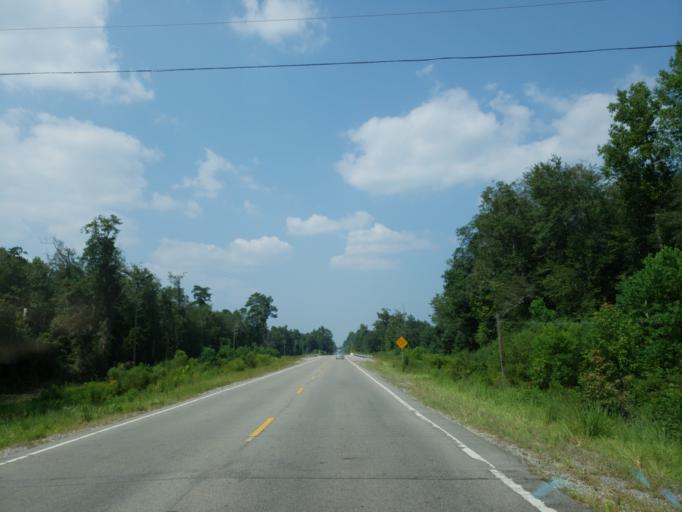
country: US
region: Mississippi
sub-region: Forrest County
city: Glendale
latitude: 31.4638
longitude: -89.2842
